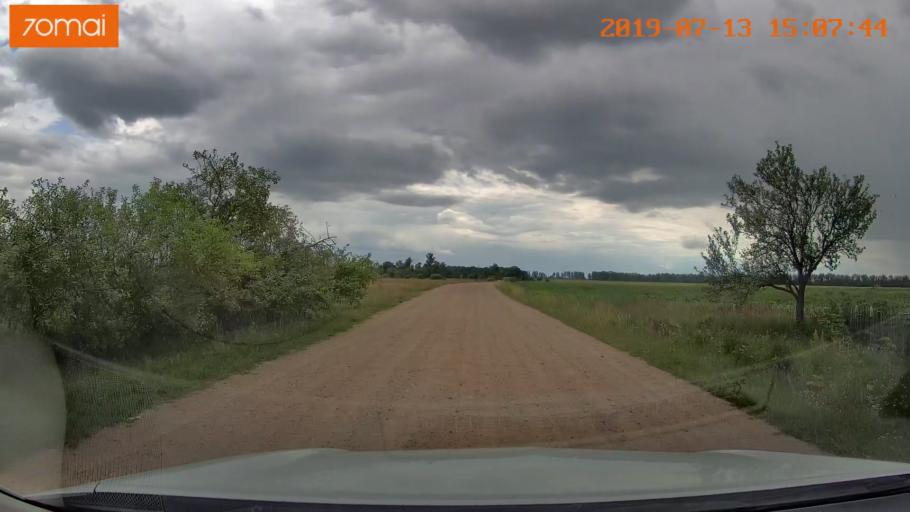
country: BY
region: Mogilev
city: Hlusha
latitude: 53.1871
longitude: 28.7570
